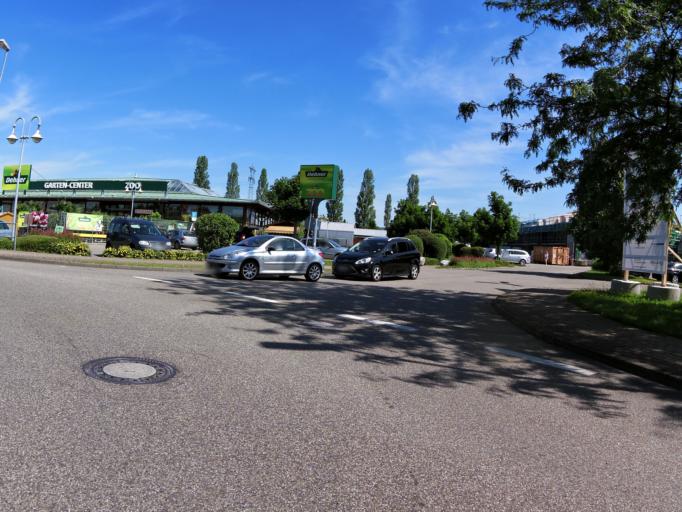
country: DE
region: Baden-Wuerttemberg
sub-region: Freiburg Region
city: Lahr
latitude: 48.3335
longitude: 7.8445
